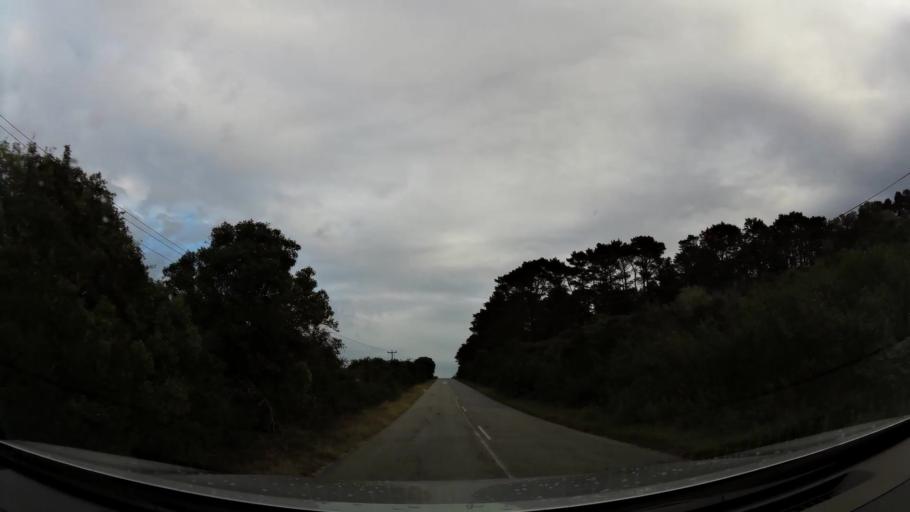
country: ZA
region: Eastern Cape
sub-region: Nelson Mandela Bay Metropolitan Municipality
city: Port Elizabeth
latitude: -34.0079
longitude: 25.4875
